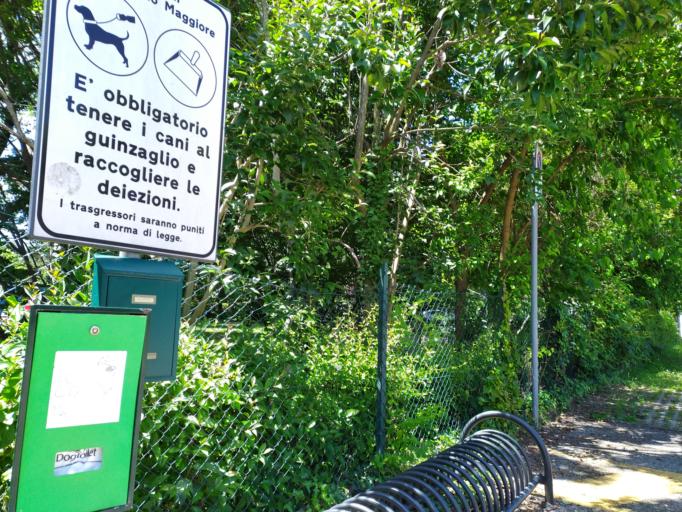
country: IT
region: Veneto
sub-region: Provincia di Vicenza
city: Tavernelle
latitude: 45.5007
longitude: 11.4415
